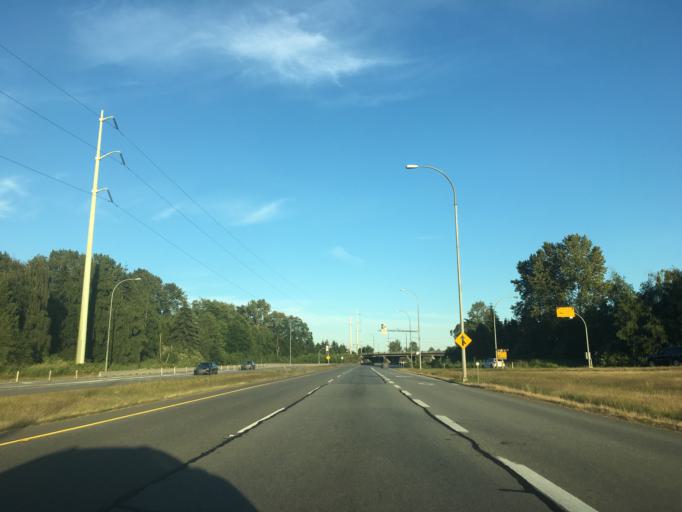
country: CA
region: British Columbia
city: Richmond
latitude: 49.1727
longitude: -123.0900
